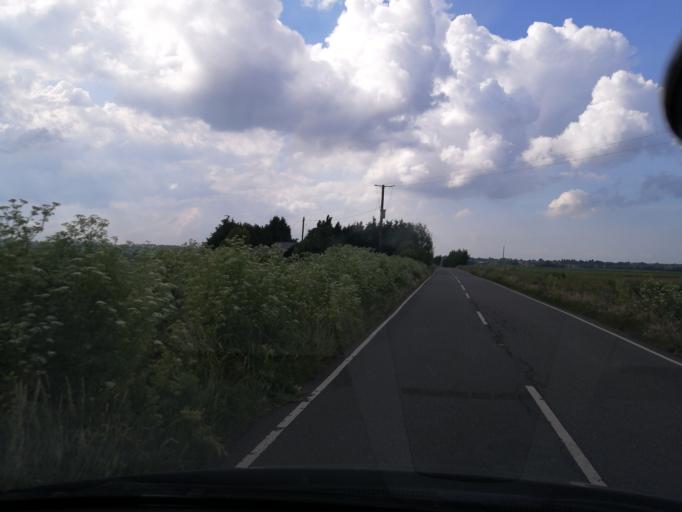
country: GB
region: England
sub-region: Cambridgeshire
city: Yaxley
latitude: 52.4971
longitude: -0.2469
